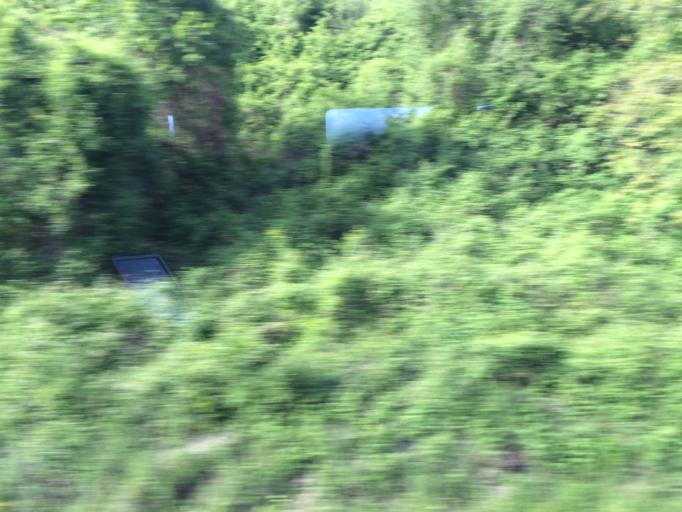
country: DE
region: Rheinland-Pfalz
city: Boppard
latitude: 50.2352
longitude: 7.6009
